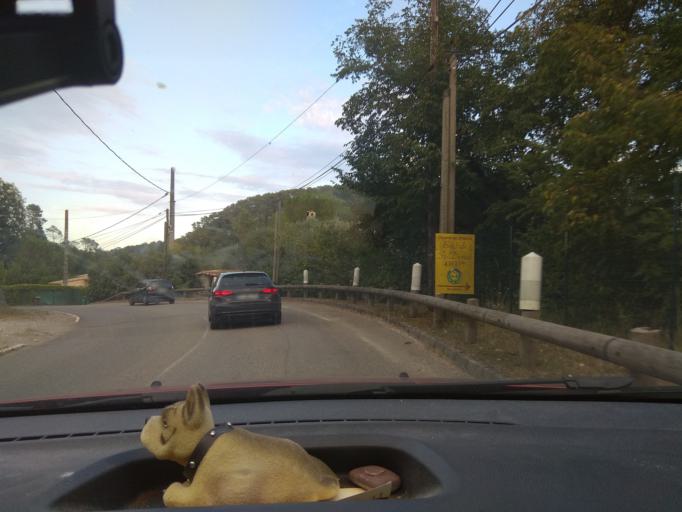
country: FR
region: Provence-Alpes-Cote d'Azur
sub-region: Departement des Alpes-Maritimes
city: La Colle-sur-Loup
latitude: 43.6823
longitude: 7.0856
